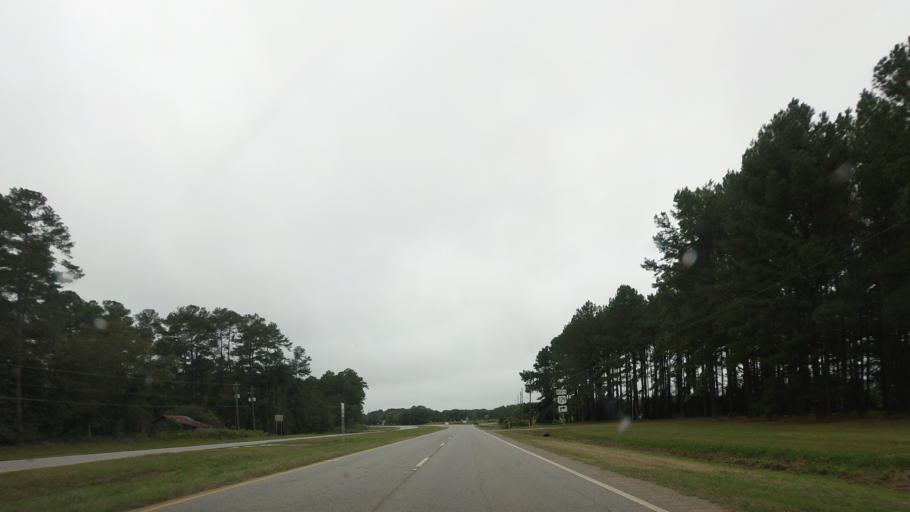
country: US
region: Georgia
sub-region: Berrien County
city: Enigma
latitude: 31.3941
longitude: -83.2357
